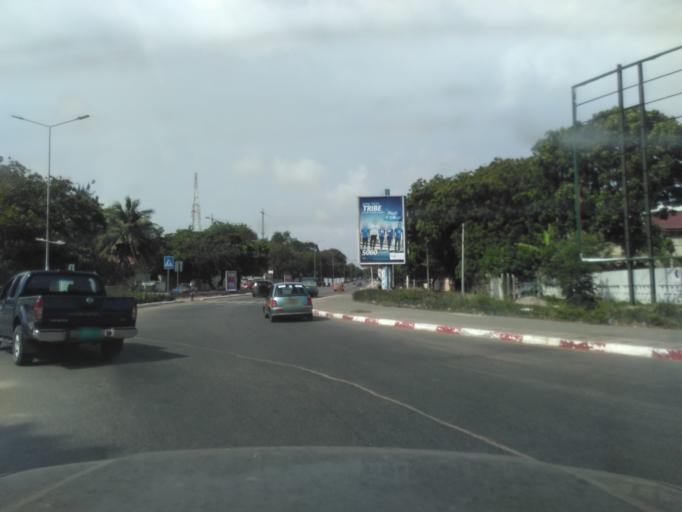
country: GH
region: Greater Accra
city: Accra
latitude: 5.5594
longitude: -0.1970
